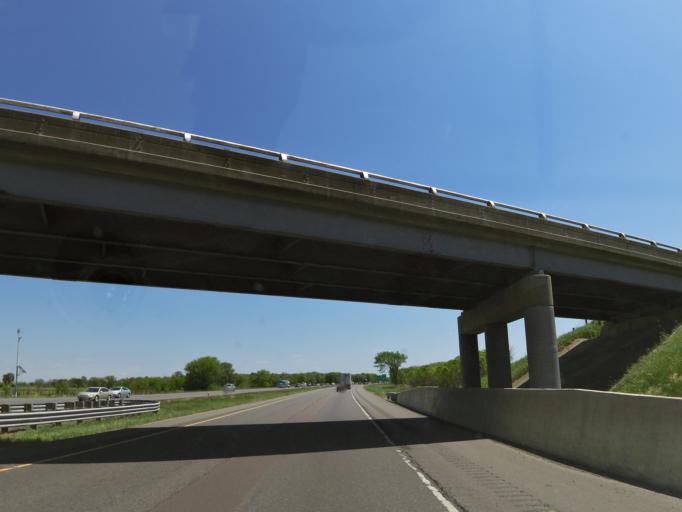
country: US
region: Wisconsin
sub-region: Juneau County
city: New Lisbon
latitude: 43.9370
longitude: -90.2969
